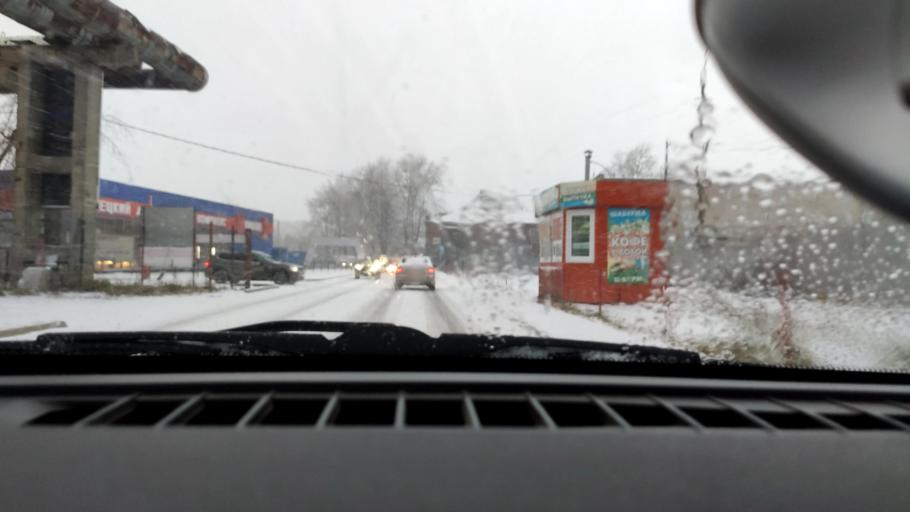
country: RU
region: Perm
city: Froly
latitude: 57.9644
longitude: 56.2721
